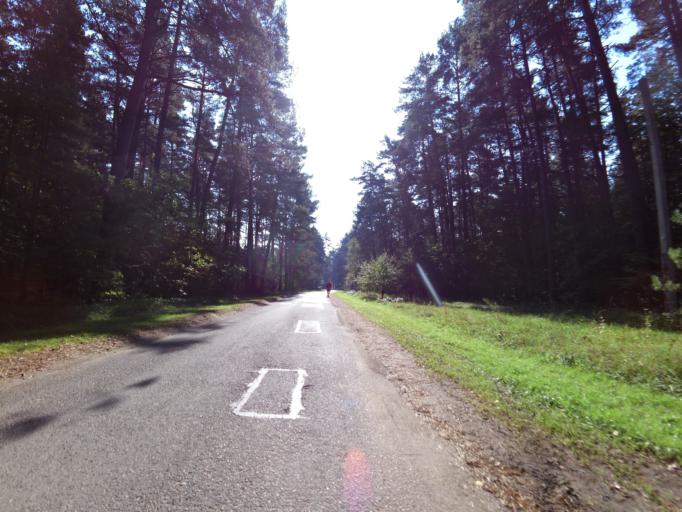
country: LT
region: Vilnius County
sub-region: Vilnius
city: Vilnius
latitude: 54.7379
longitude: 25.3062
